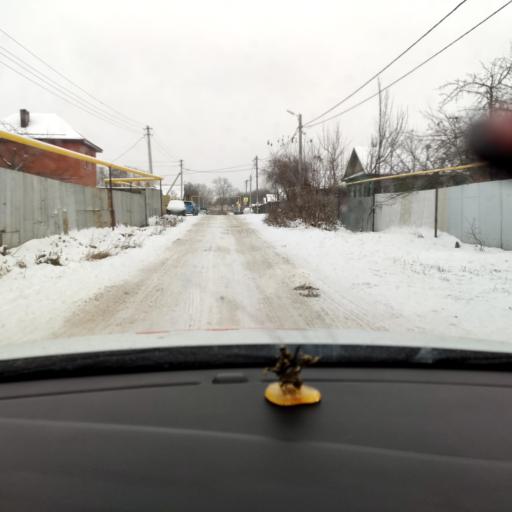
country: RU
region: Tatarstan
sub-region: Gorod Kazan'
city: Kazan
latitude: 55.7390
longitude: 49.0980
